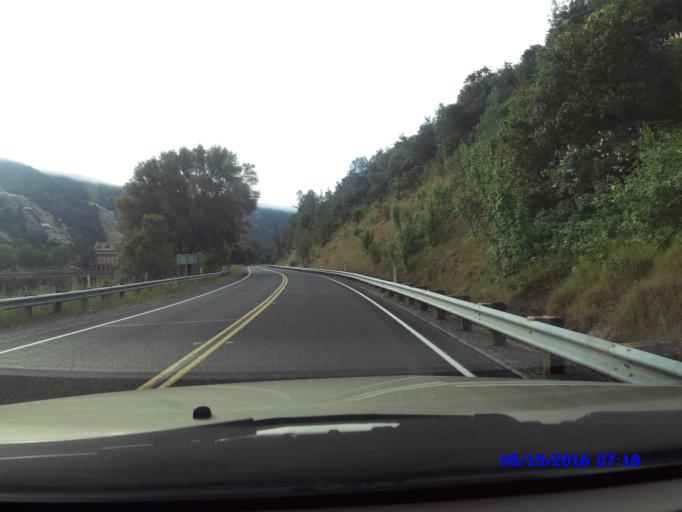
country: US
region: California
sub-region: Tuolumne County
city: Tuolumne City
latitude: 37.8100
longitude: -120.3059
